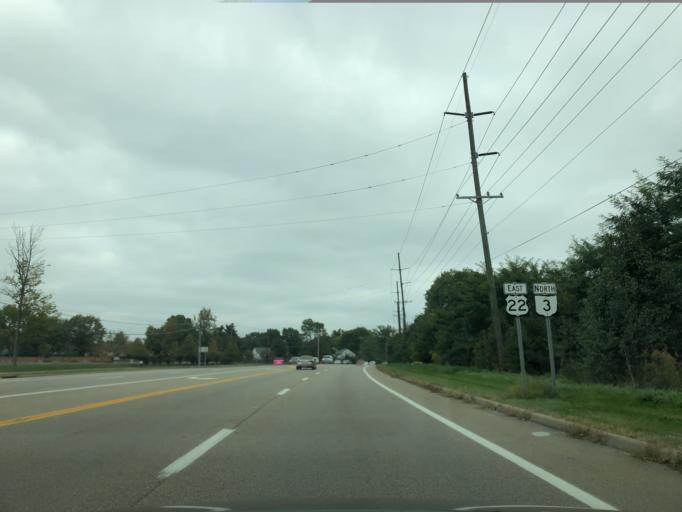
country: US
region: Ohio
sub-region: Hamilton County
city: Sixteen Mile Stand
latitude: 39.2831
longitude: -84.3153
